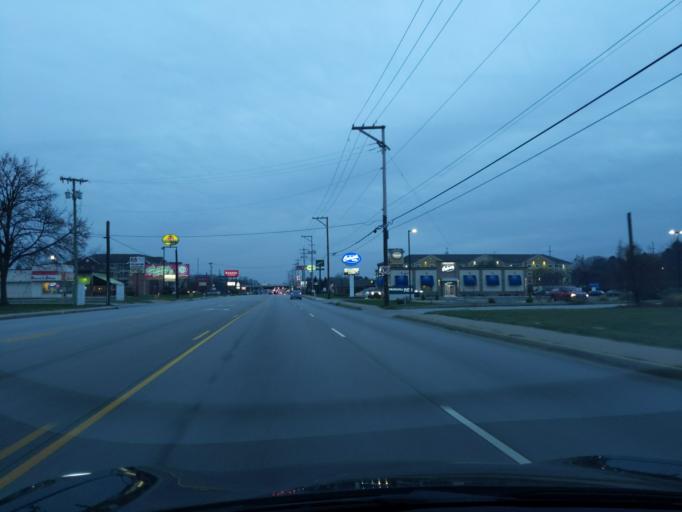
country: US
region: Indiana
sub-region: Saint Joseph County
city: Georgetown
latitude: 41.7266
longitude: -86.2506
